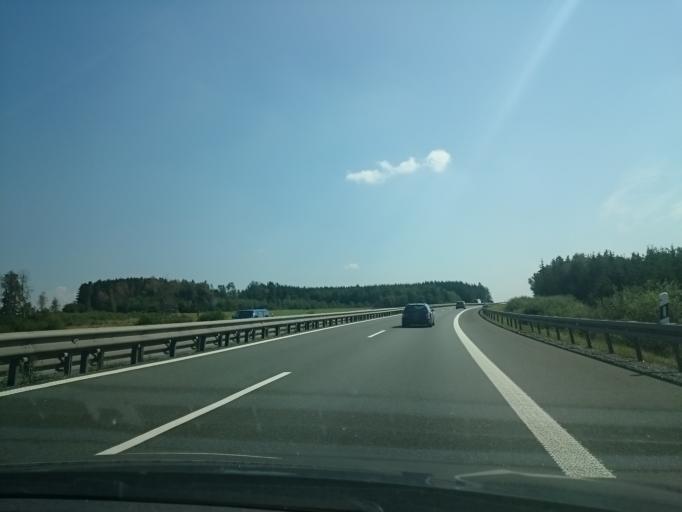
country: DE
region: Bavaria
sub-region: Upper Franconia
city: Feilitzsch
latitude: 50.3768
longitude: 11.9196
